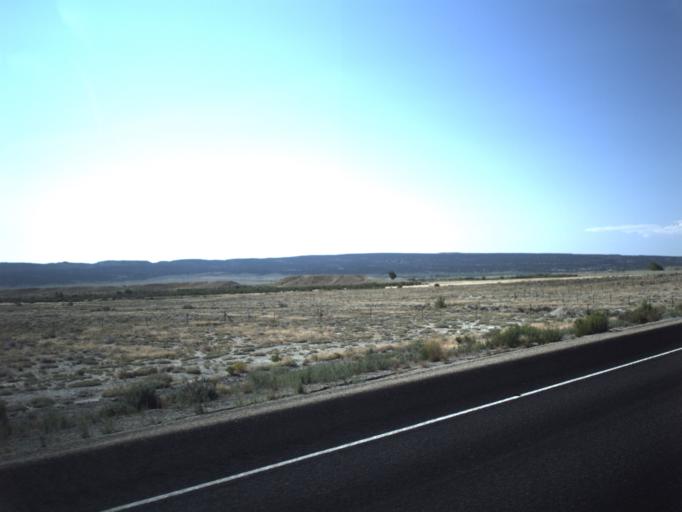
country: US
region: Utah
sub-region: Emery County
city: Ferron
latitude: 38.9780
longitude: -111.1757
